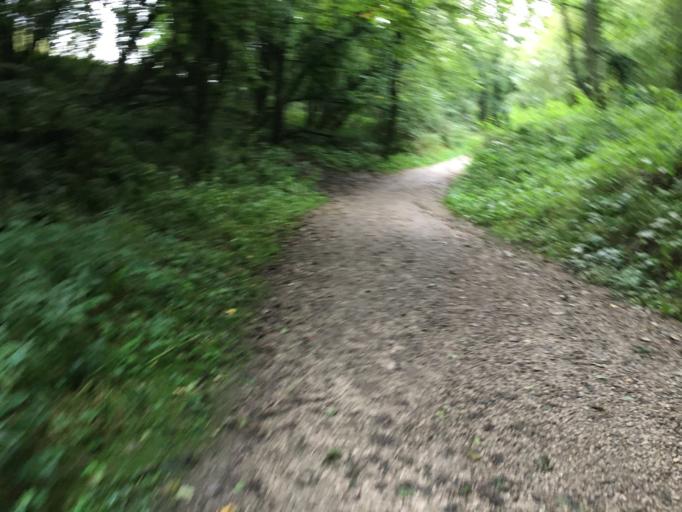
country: GB
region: England
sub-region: North Yorkshire
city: Sleights
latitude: 54.4047
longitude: -0.7271
